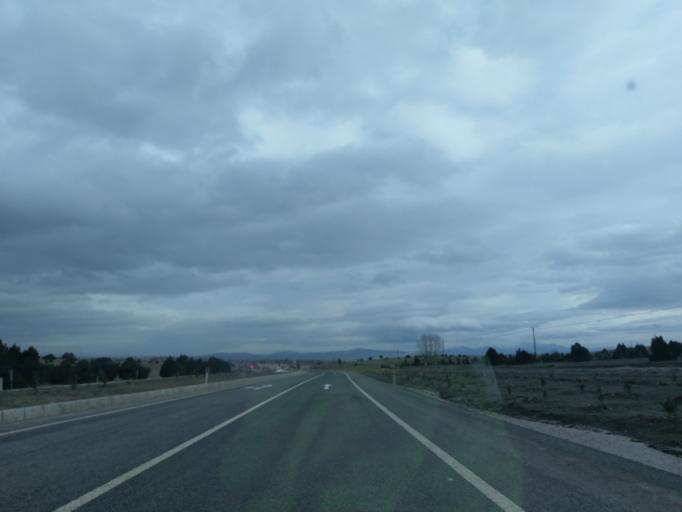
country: TR
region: Kuetahya
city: Aslanapa
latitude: 39.2300
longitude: 29.7677
